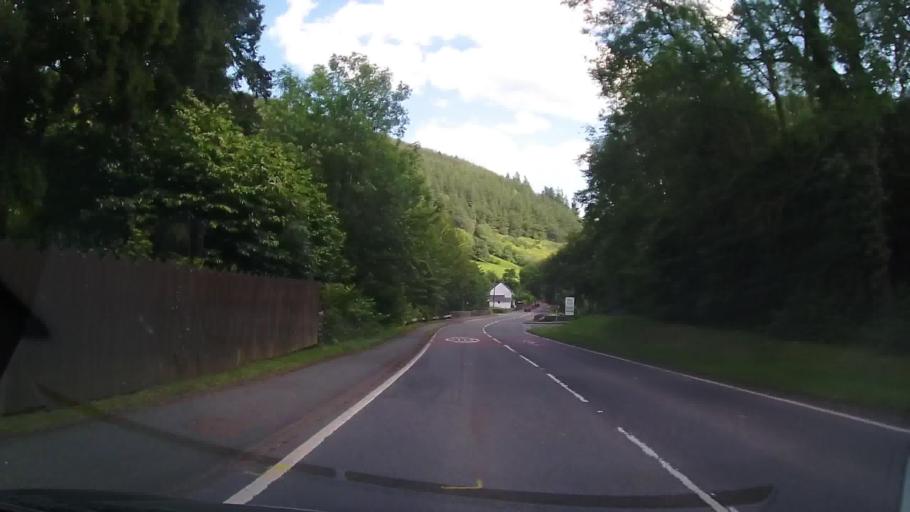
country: GB
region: Wales
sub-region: Gwynedd
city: Corris
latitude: 52.7120
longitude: -3.6902
